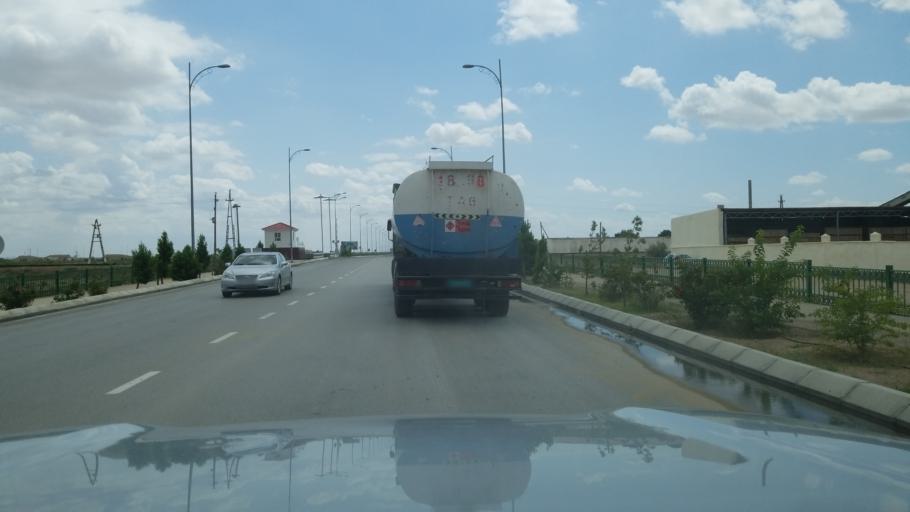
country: TM
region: Balkan
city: Balkanabat
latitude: 39.4911
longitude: 54.3780
